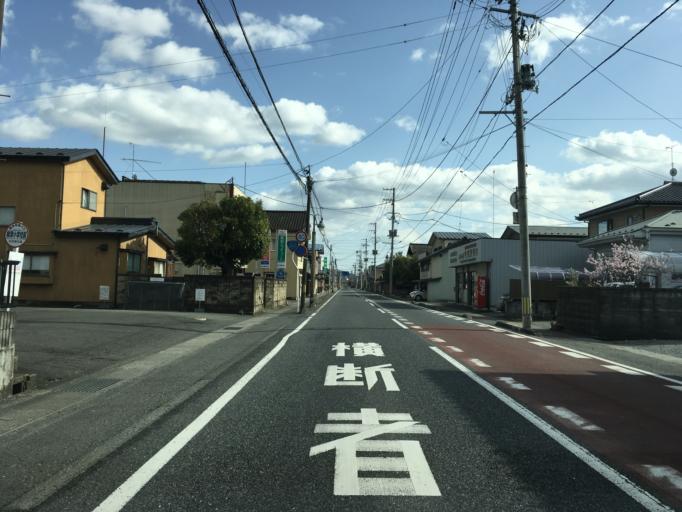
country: JP
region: Miyagi
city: Wakuya
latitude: 38.6152
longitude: 141.2999
